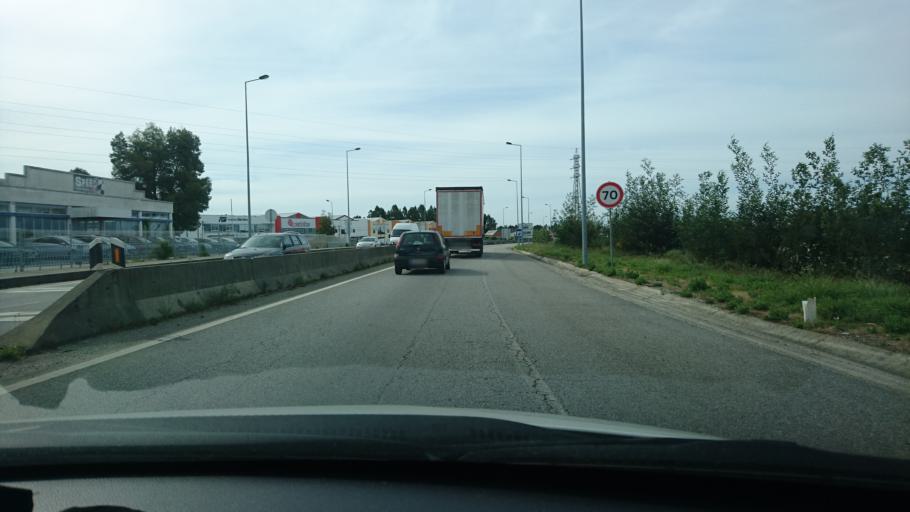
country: PT
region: Aveiro
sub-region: Albergaria-A-Velha
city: Albergaria-a-Velha
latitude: 40.7120
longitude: -8.4829
